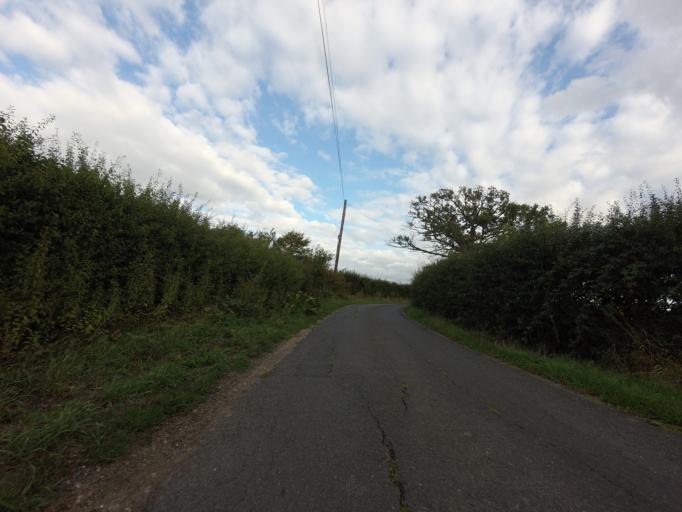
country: GB
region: England
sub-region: Kent
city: Staplehurst
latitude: 51.2059
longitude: 0.5403
